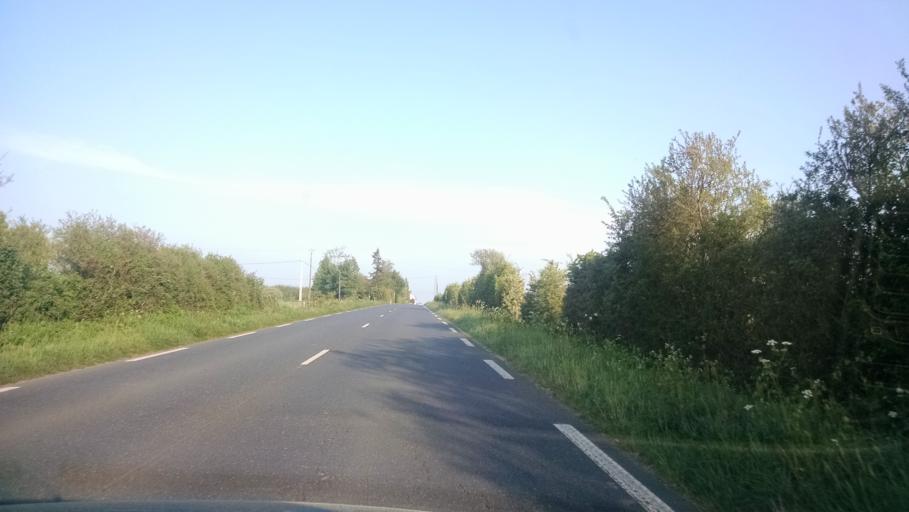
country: FR
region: Pays de la Loire
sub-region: Departement de la Loire-Atlantique
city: Getigne
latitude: 47.0704
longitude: -1.2159
